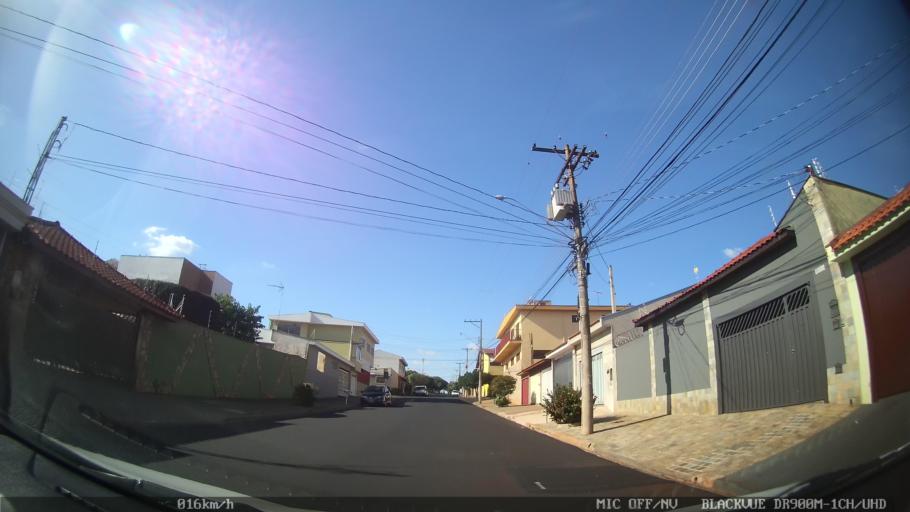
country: BR
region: Sao Paulo
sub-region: Ribeirao Preto
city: Ribeirao Preto
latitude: -21.1759
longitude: -47.7758
